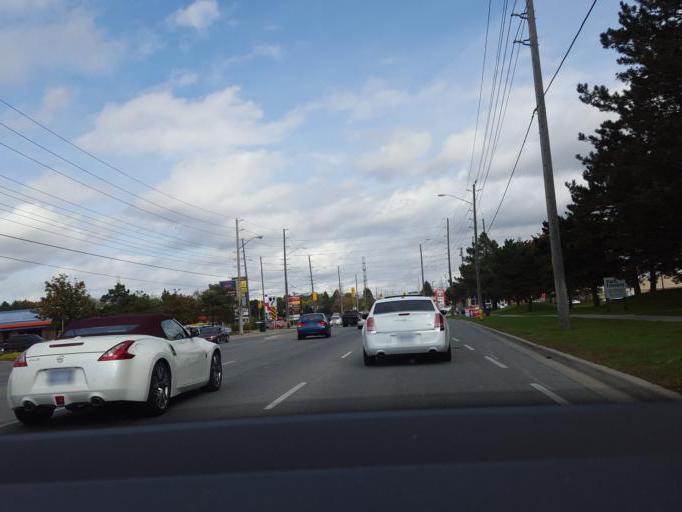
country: CA
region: Ontario
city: Oshawa
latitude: 43.9347
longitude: -78.8707
